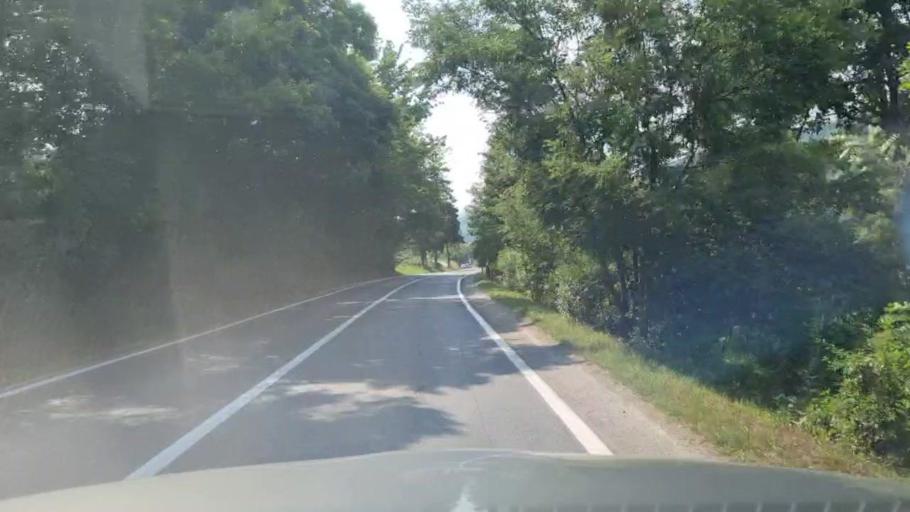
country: BA
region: Federation of Bosnia and Herzegovina
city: Olovo
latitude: 44.1267
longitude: 18.6108
